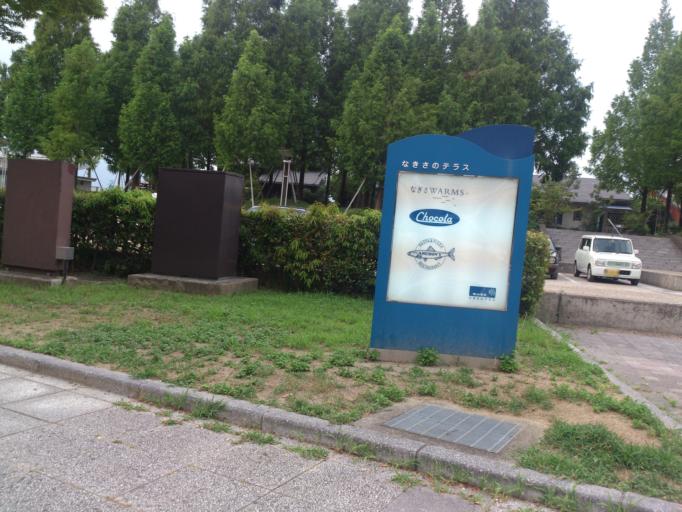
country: JP
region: Shiga Prefecture
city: Otsu-shi
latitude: 35.0070
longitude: 135.8755
